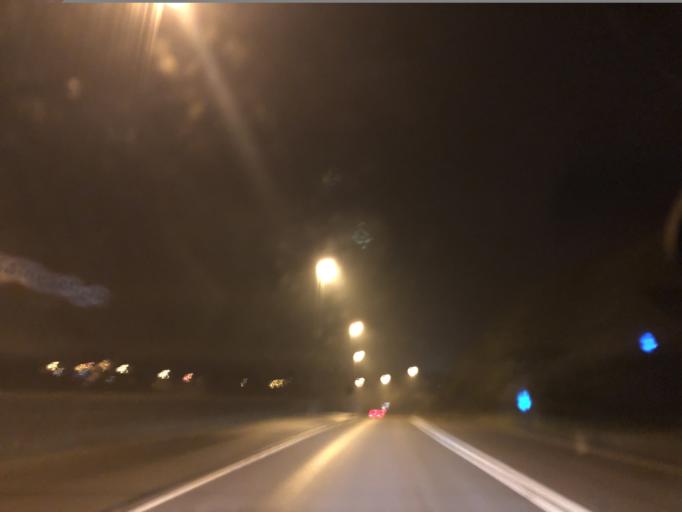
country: GB
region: England
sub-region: Borough of Oldham
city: Shaw
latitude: 53.5713
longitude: -2.0662
